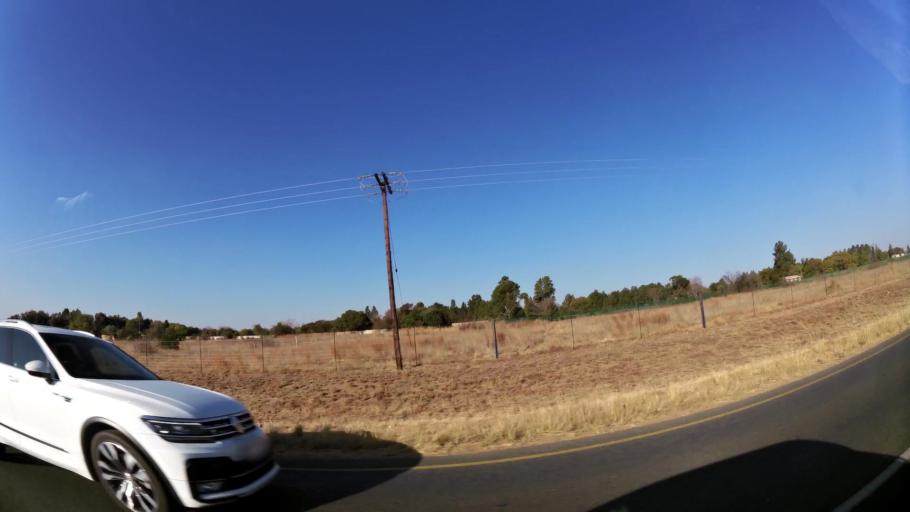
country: ZA
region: Gauteng
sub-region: West Rand District Municipality
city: Muldersdriseloop
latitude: -26.0181
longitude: 27.9092
